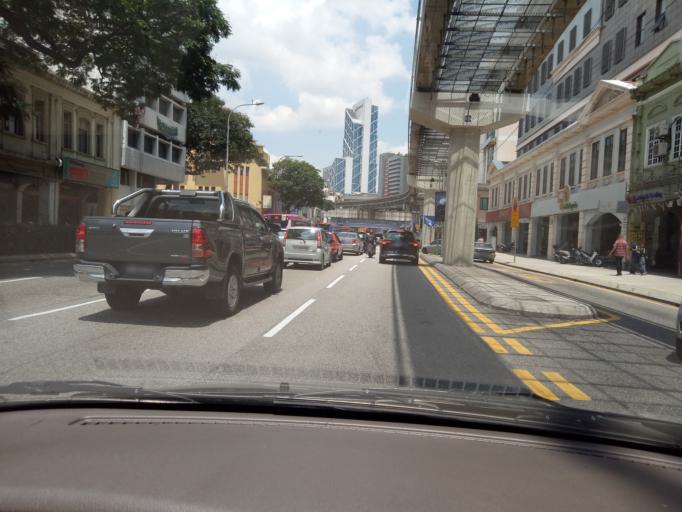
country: MY
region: Kuala Lumpur
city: Kuala Lumpur
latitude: 3.1611
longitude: 101.6974
